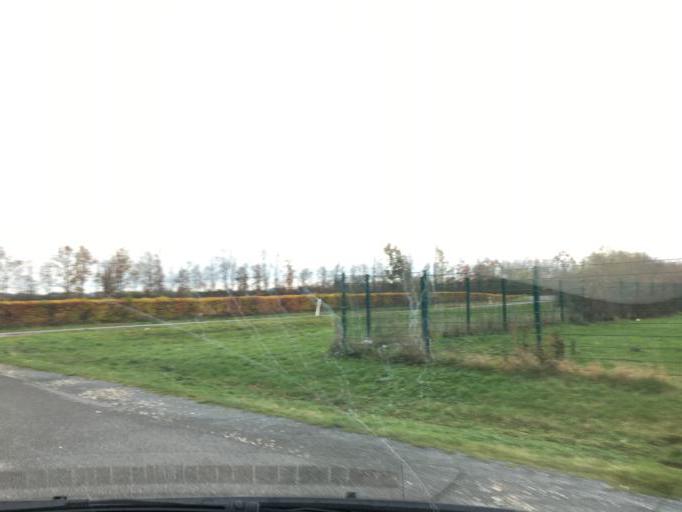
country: DE
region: North Rhine-Westphalia
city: Julich
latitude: 50.9271
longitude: 6.3340
